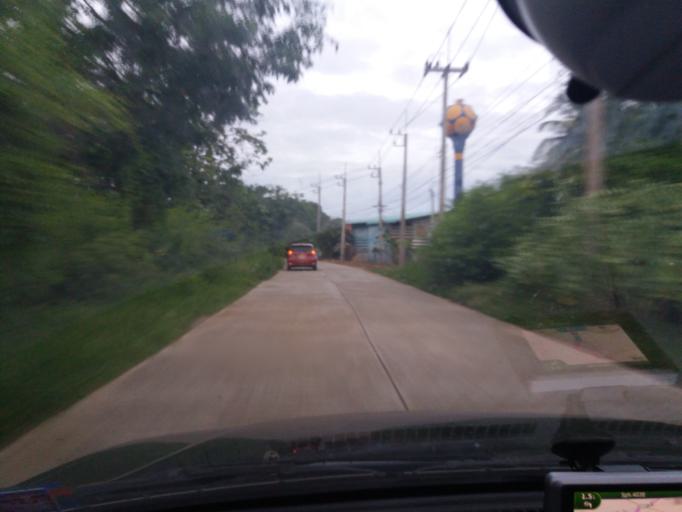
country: TH
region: Suphan Buri
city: Ban Sam Chuk
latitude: 14.7250
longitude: 100.0726
